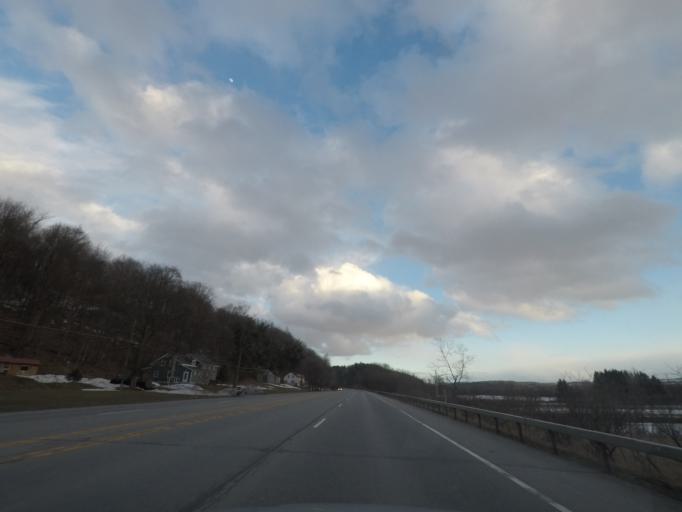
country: US
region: New York
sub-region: Herkimer County
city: Little Falls
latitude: 43.0285
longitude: -74.7949
